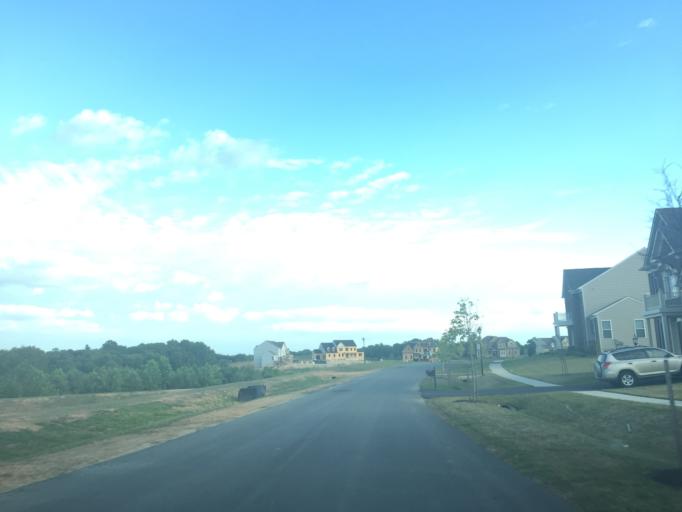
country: US
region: Maryland
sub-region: Montgomery County
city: Redland
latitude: 39.1306
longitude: -77.1131
